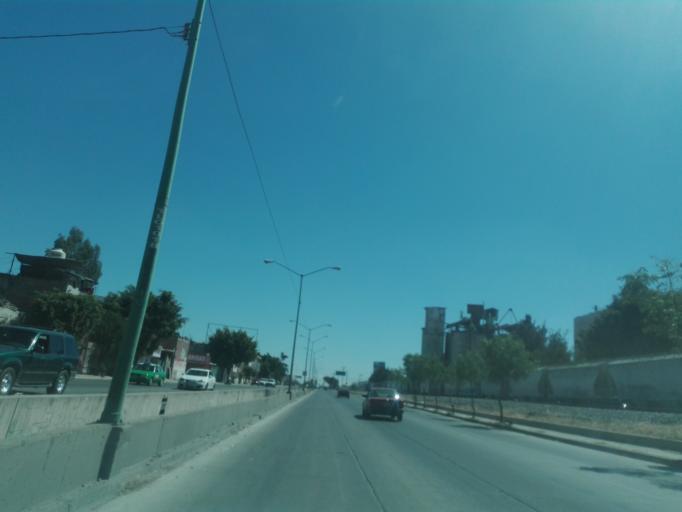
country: MX
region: Guanajuato
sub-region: Leon
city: San Jose de Duran (Los Troncoso)
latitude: 21.0862
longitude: -101.6694
